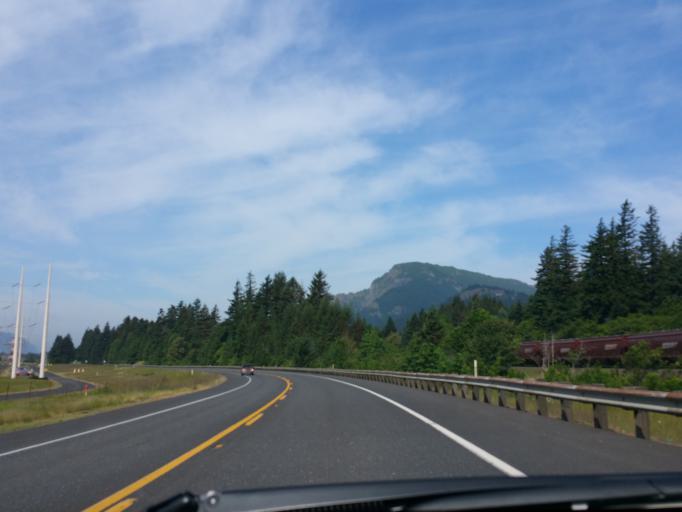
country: US
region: Oregon
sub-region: Hood River County
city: Cascade Locks
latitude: 45.6521
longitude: -121.9415
